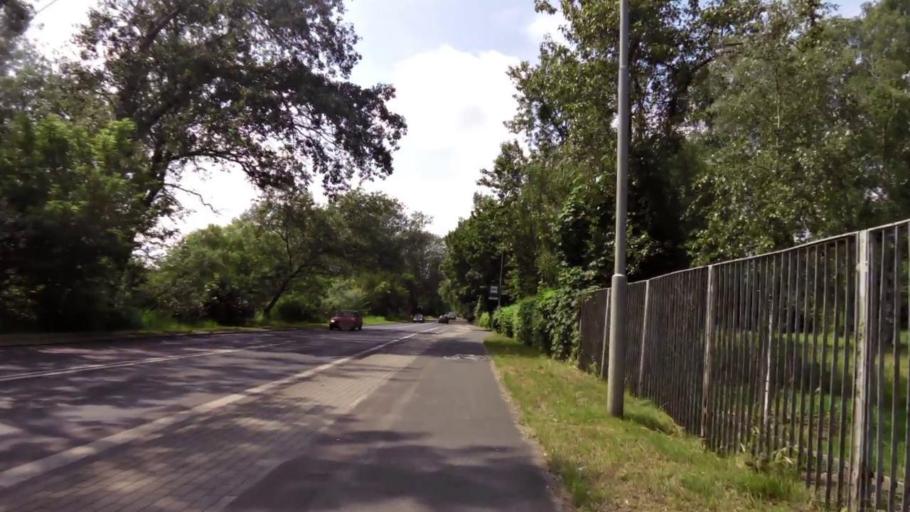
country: PL
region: West Pomeranian Voivodeship
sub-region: Szczecin
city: Szczecin
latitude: 53.3961
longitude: 14.6272
